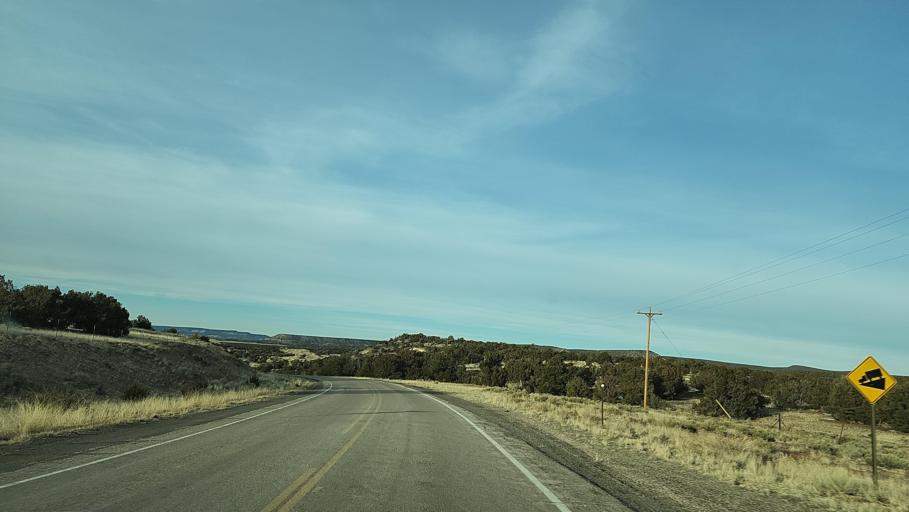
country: US
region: New Mexico
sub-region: McKinley County
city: Black Rock
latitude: 34.4155
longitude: -108.4309
